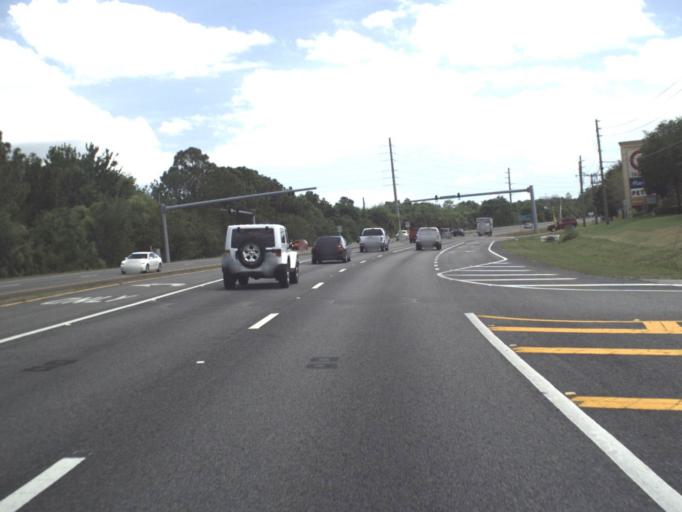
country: US
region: Florida
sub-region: Brevard County
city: Titusville
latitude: 28.5535
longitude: -80.8417
